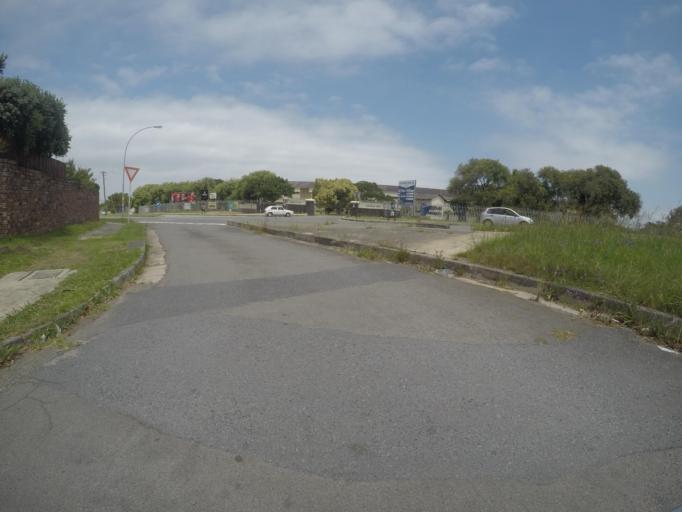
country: ZA
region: Eastern Cape
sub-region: Buffalo City Metropolitan Municipality
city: East London
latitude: -32.9984
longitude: 27.9163
